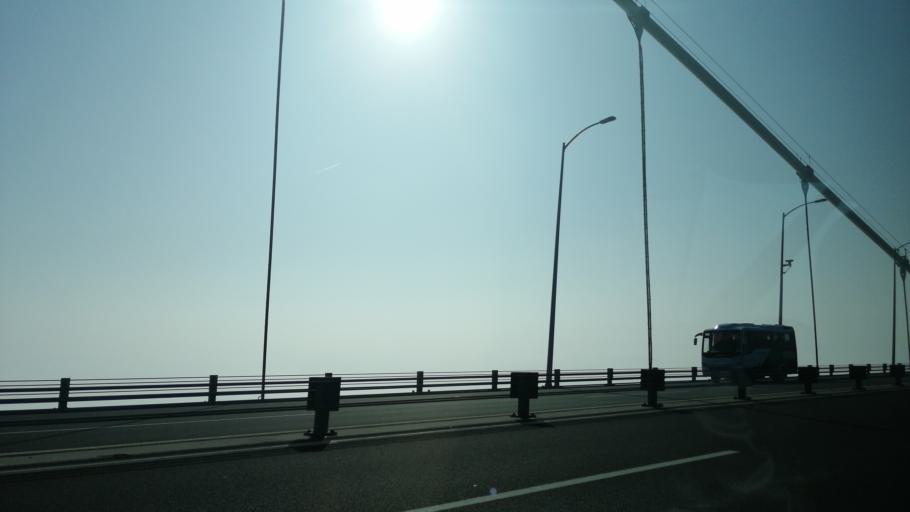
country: TR
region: Yalova
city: Altinova
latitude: 40.7457
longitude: 29.5142
